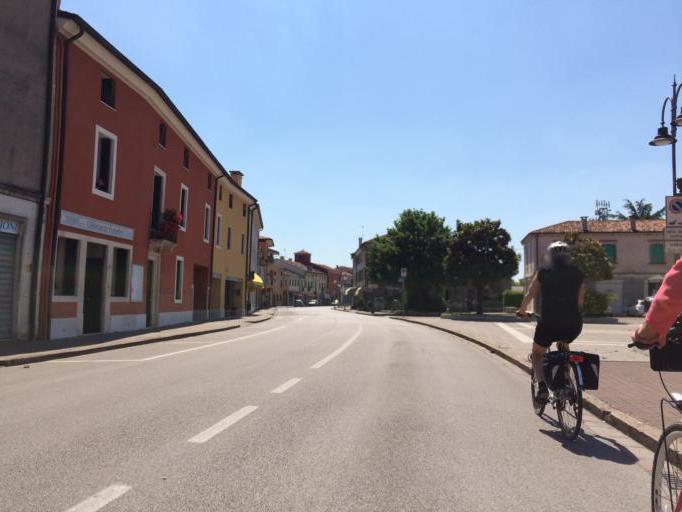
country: IT
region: Veneto
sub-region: Provincia di Vicenza
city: Sossano
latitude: 45.3579
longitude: 11.5090
